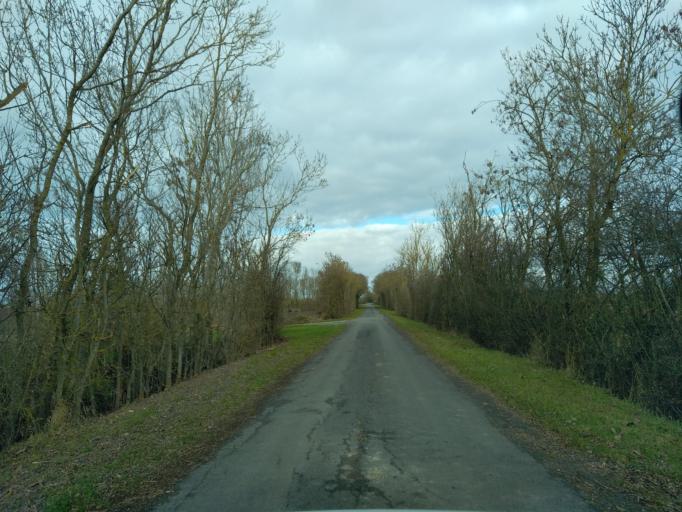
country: FR
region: Pays de la Loire
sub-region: Departement de la Vendee
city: Maillezais
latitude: 46.3334
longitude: -0.7908
